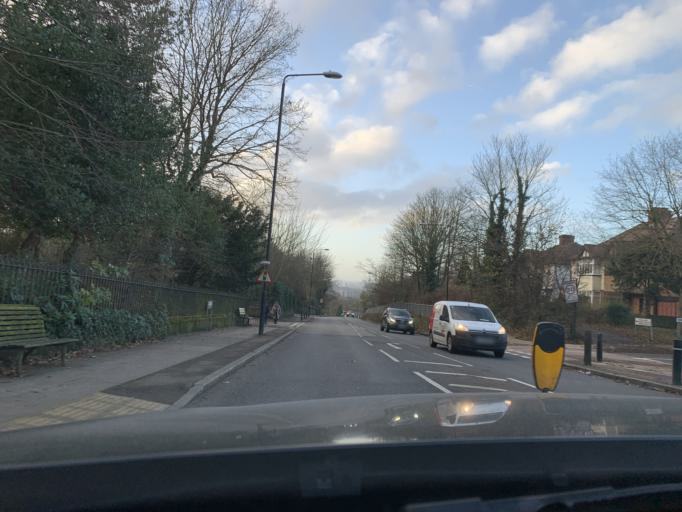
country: GB
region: England
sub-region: Greater London
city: Woolwich
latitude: 51.4696
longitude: 0.0640
